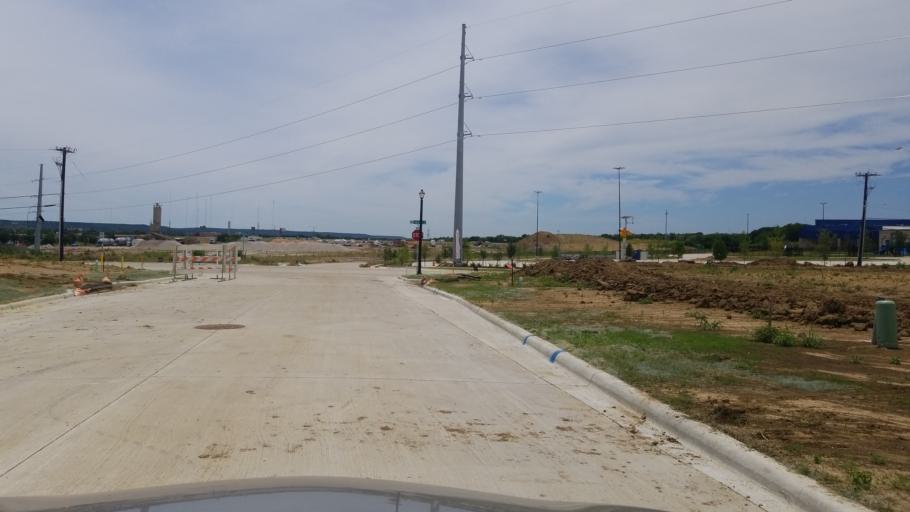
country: US
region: Texas
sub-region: Dallas County
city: Grand Prairie
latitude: 32.6775
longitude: -96.9868
